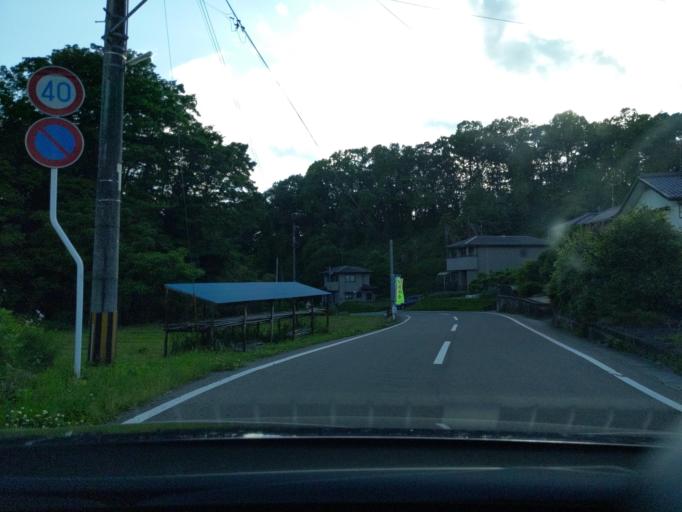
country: JP
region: Fukushima
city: Koriyama
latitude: 37.4209
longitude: 140.4304
